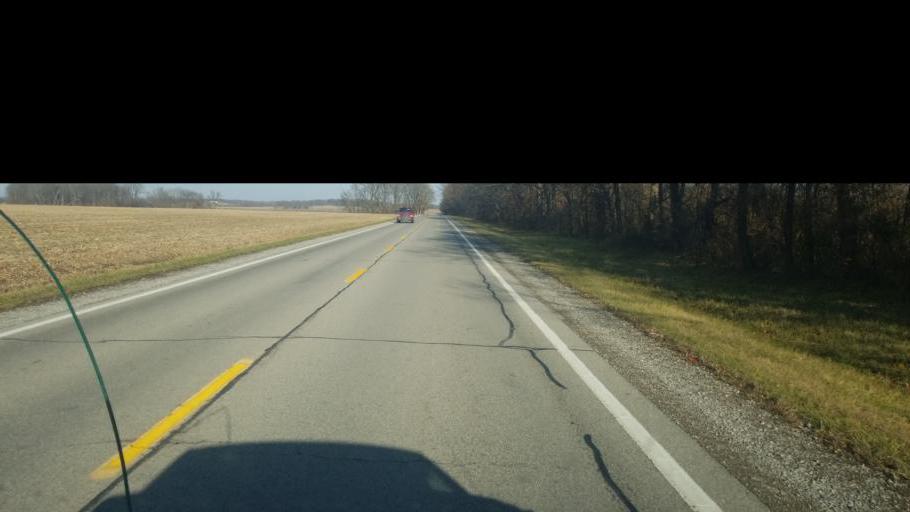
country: US
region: Illinois
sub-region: Wabash County
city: Mount Carmel
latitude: 38.3664
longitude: -87.8491
